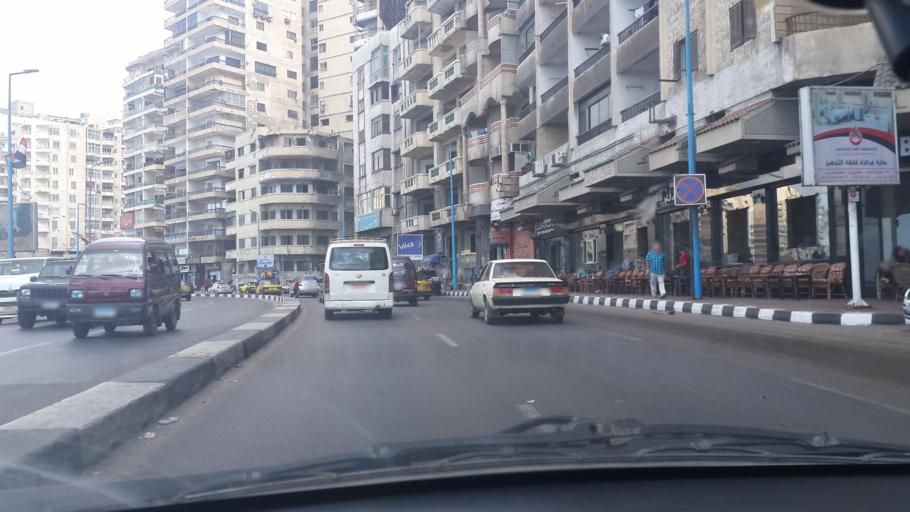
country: EG
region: Alexandria
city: Alexandria
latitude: 31.2707
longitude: 29.9954
